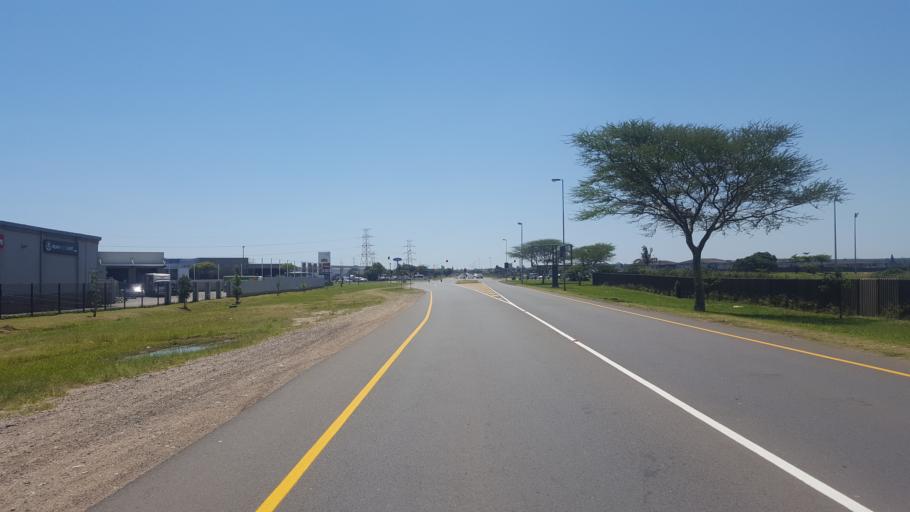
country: ZA
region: KwaZulu-Natal
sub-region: uThungulu District Municipality
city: Richards Bay
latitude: -28.7464
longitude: 32.0522
